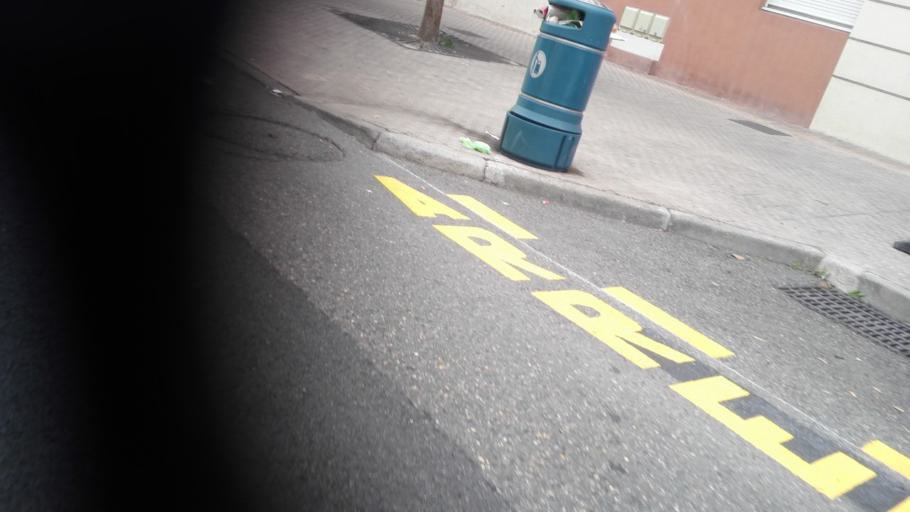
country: FR
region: Provence-Alpes-Cote d'Azur
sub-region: Departement des Alpes-Maritimes
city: Menton
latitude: 43.7713
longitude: 7.4954
